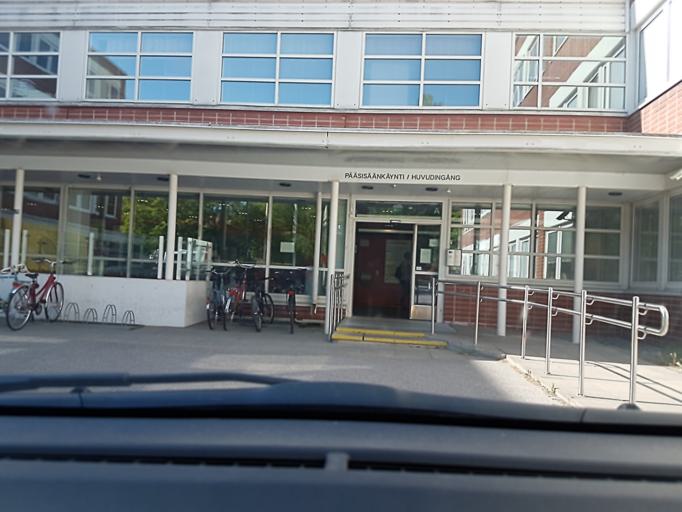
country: FI
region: Uusimaa
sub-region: Helsinki
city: Vantaa
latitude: 60.3197
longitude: 25.0595
